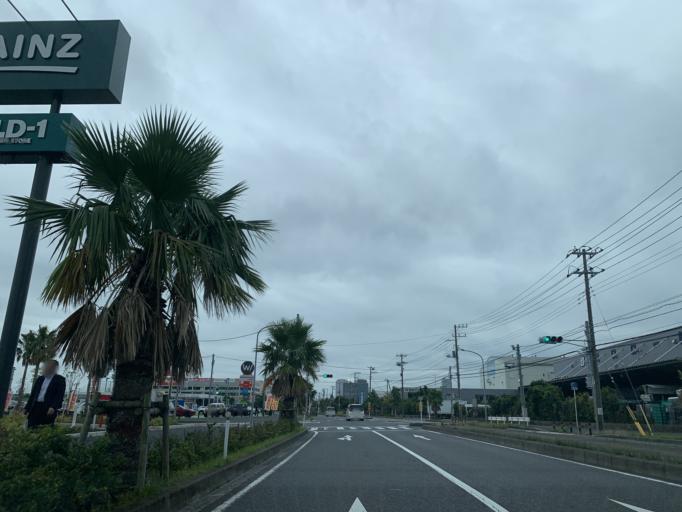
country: JP
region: Chiba
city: Funabashi
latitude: 35.6623
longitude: 140.0169
